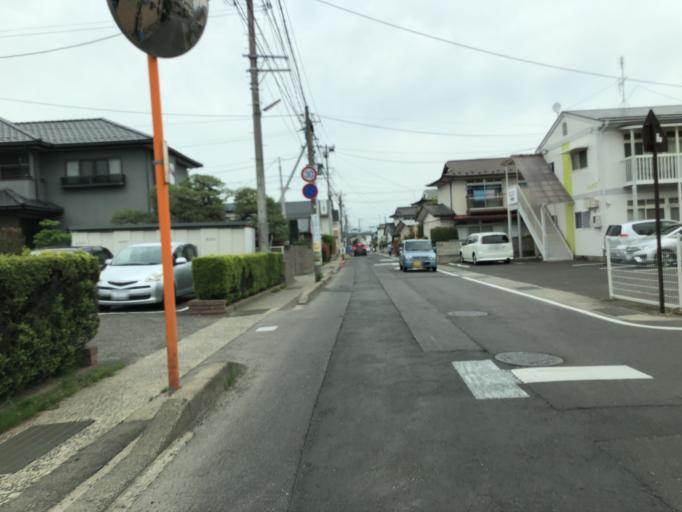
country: JP
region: Fukushima
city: Fukushima-shi
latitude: 37.7899
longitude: 140.4846
